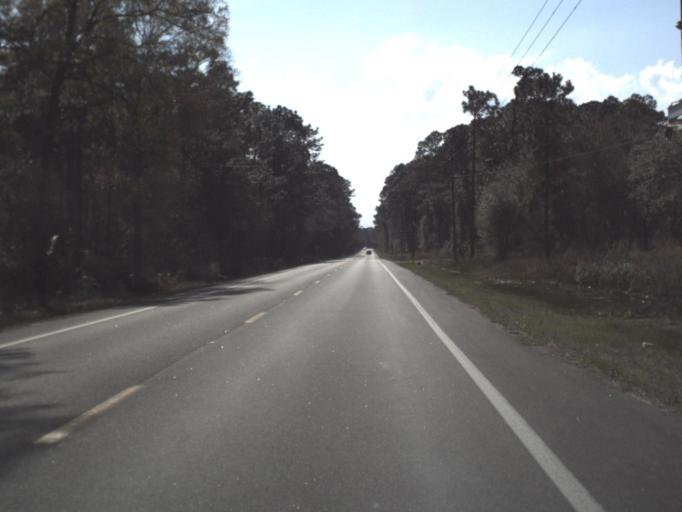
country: US
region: Florida
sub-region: Wakulla County
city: Crawfordville
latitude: 30.0809
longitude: -84.3942
